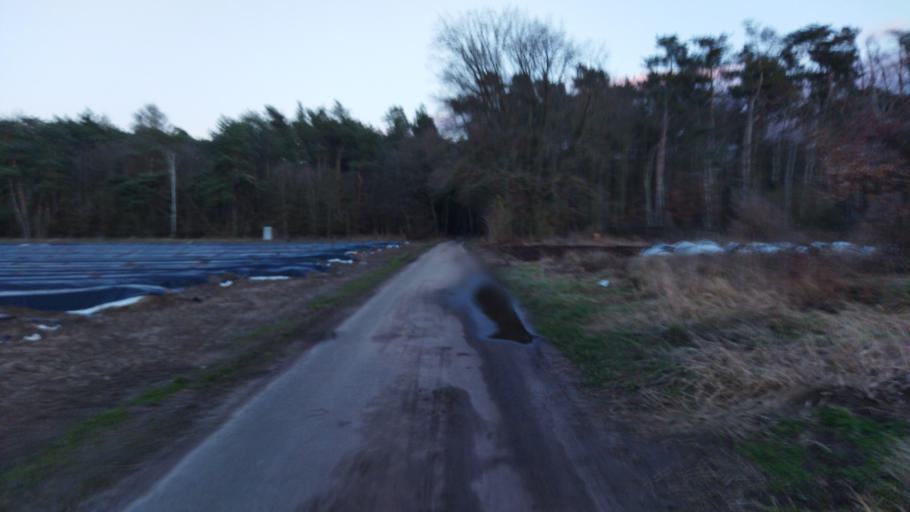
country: DE
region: Rheinland-Pfalz
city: Hanhofen
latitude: 49.3267
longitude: 8.3436
